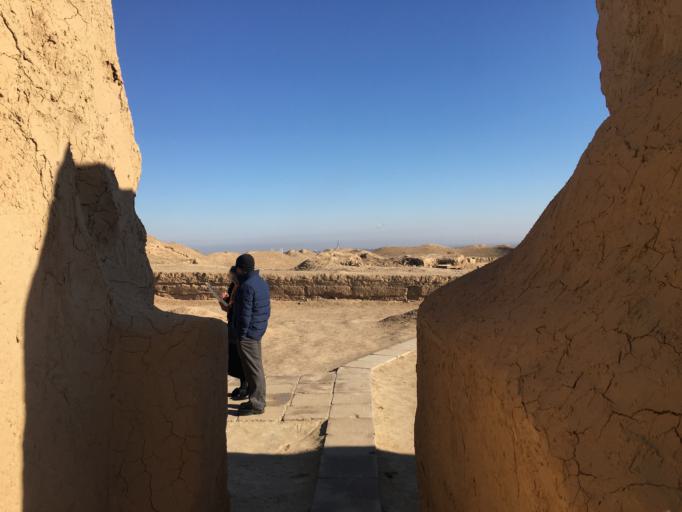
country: TM
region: Ahal
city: Abadan
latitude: 37.9517
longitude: 58.2102
